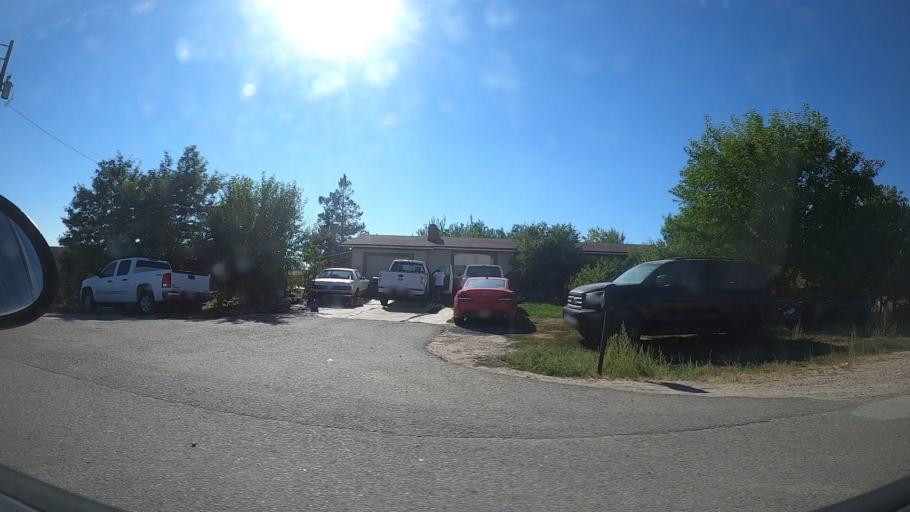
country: US
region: Idaho
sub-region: Canyon County
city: Nampa
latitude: 43.6049
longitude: -116.6128
